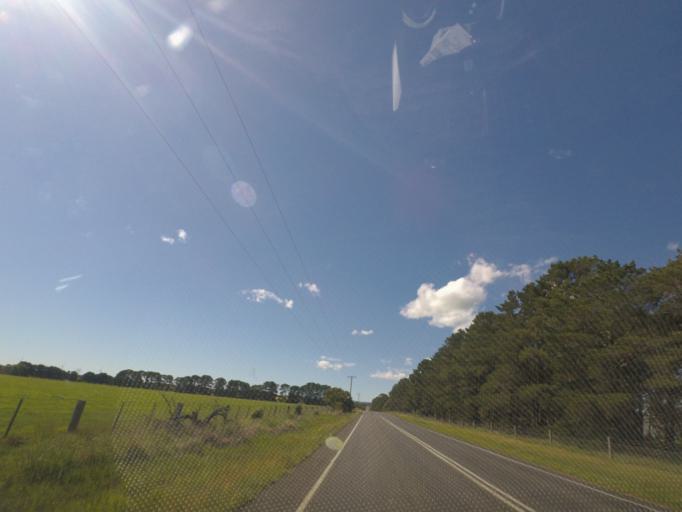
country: AU
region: Victoria
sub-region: Moorabool
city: Bacchus Marsh
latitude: -37.6746
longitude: 144.2278
